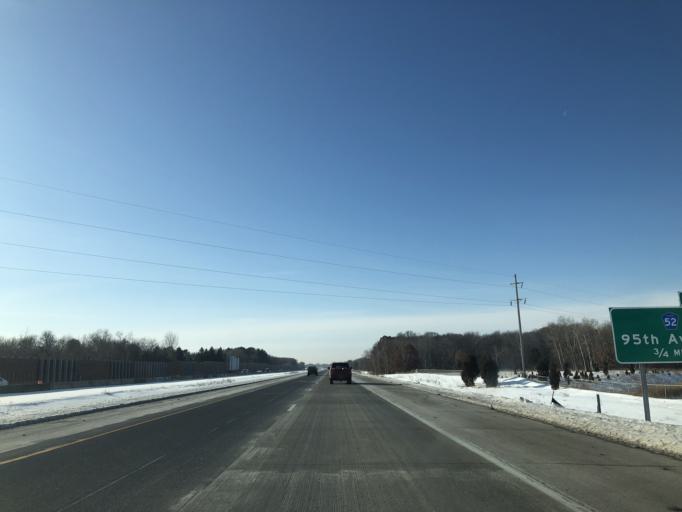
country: US
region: Minnesota
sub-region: Anoka County
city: Lexington
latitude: 45.1537
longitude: -93.1715
